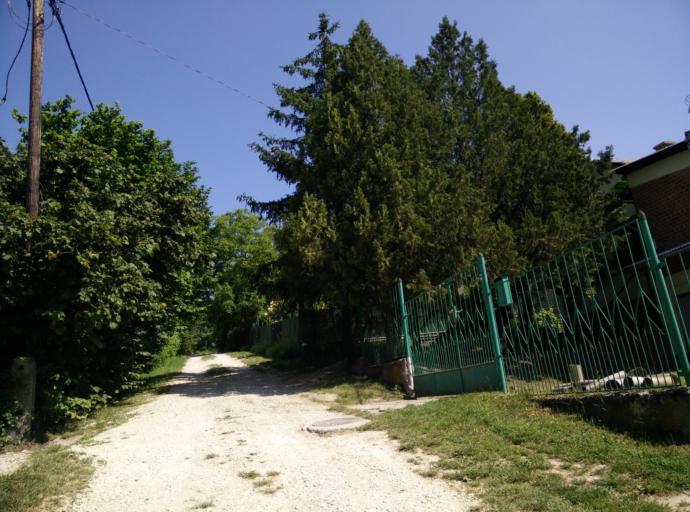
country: HU
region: Pest
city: Biatorbagy
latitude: 47.4701
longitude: 18.8396
